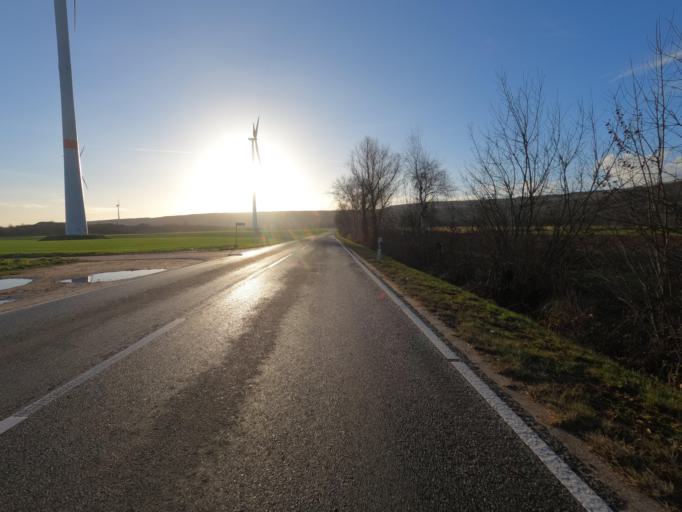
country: DE
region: North Rhine-Westphalia
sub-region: Regierungsbezirk Koln
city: Niederzier
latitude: 50.9462
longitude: 6.4802
